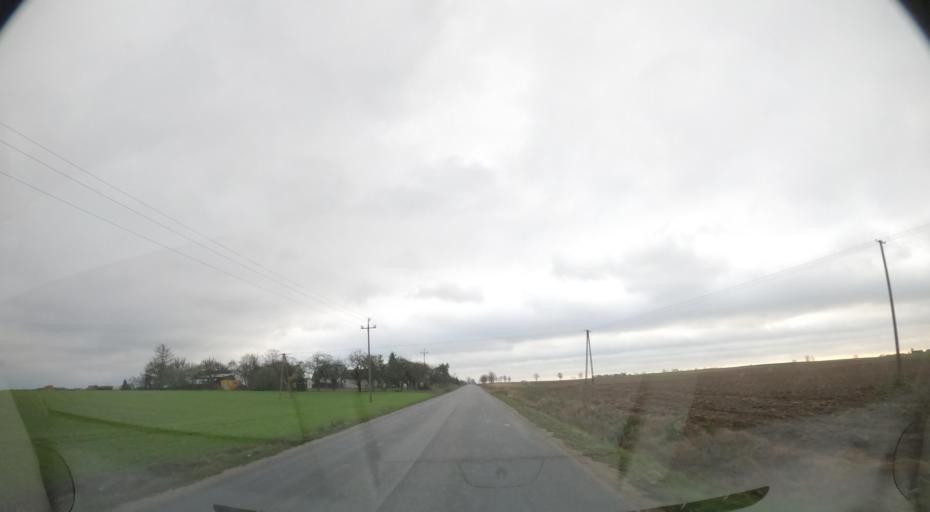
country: PL
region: Greater Poland Voivodeship
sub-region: Powiat pilski
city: Lobzenica
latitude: 53.2182
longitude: 17.3454
